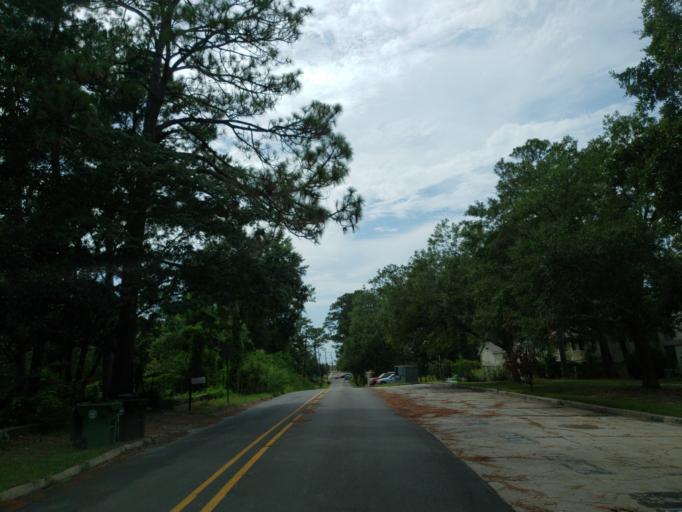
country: US
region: Mississippi
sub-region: Lamar County
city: Arnold Line
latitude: 31.3285
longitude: -89.3432
